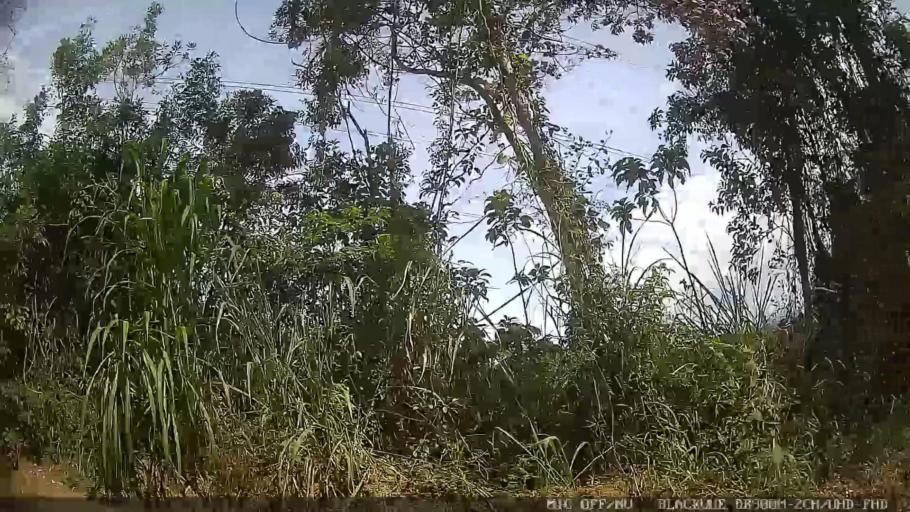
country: BR
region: Sao Paulo
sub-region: Mogi das Cruzes
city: Mogi das Cruzes
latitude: -23.6475
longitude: -46.2202
